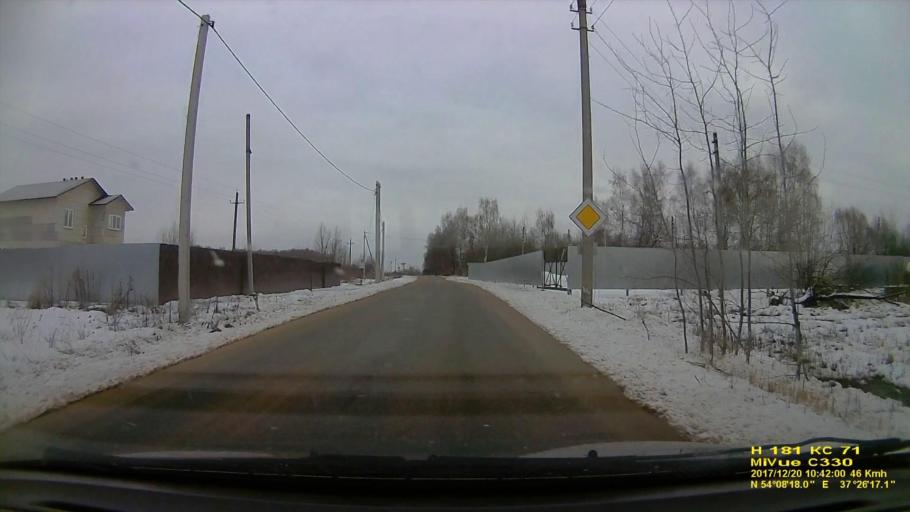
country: RU
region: Tula
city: Kosaya Gora
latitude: 54.1385
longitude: 37.4381
